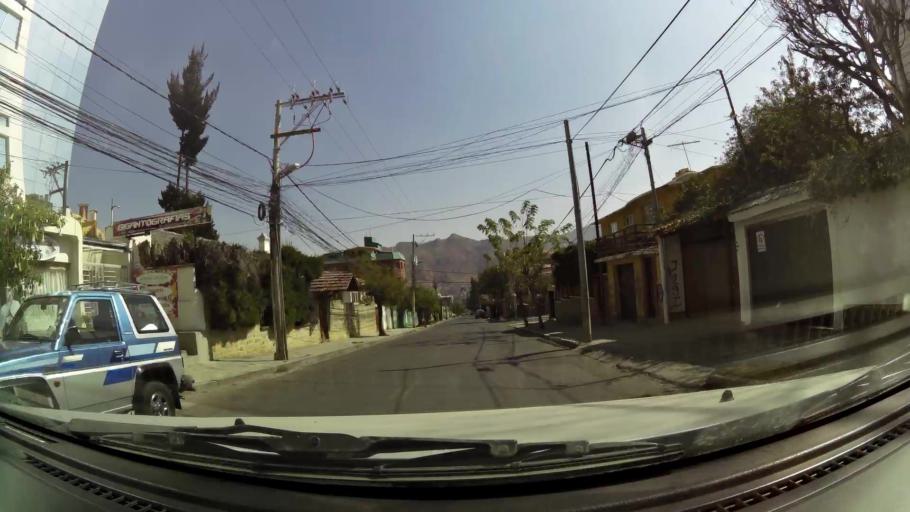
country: BO
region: La Paz
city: La Paz
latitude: -16.5401
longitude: -68.0795
